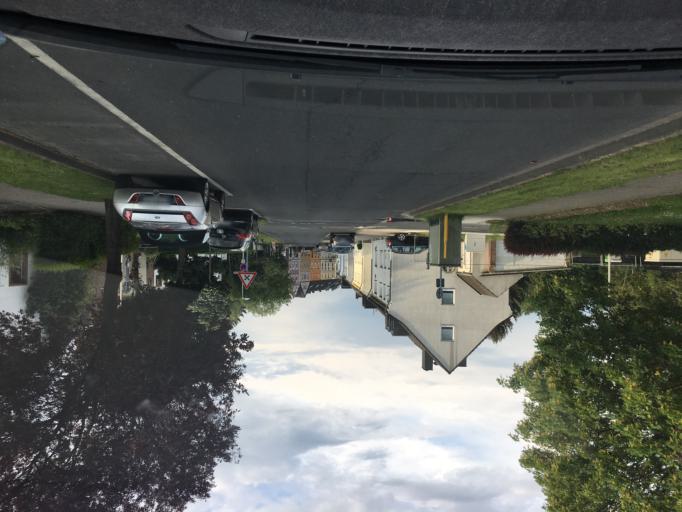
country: DE
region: North Rhine-Westphalia
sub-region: Regierungsbezirk Koln
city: Dueren
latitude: 50.8170
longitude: 6.4768
